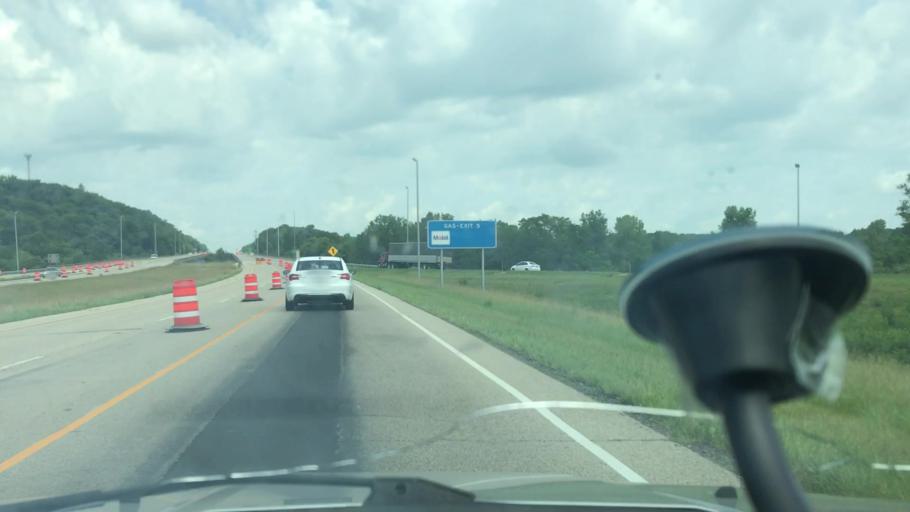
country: US
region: Illinois
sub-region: Peoria County
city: Bartonville
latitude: 40.6590
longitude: -89.6458
